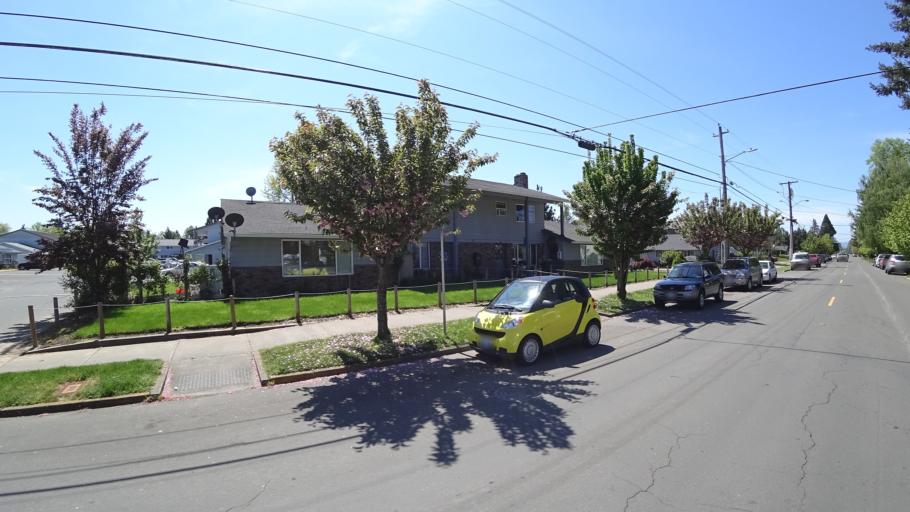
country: US
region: Oregon
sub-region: Washington County
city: Hillsboro
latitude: 45.5174
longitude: -122.9665
